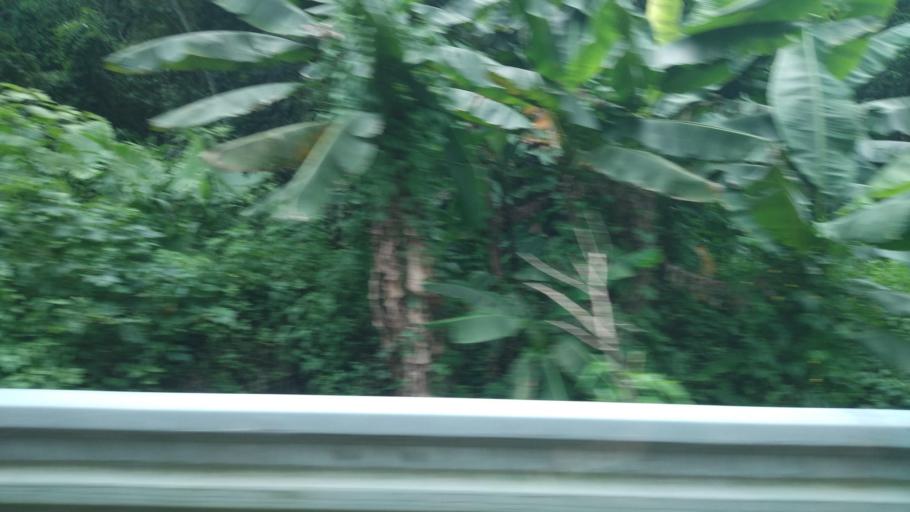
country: TW
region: Taipei
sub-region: Taipei
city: Banqiao
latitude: 24.9212
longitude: 121.4248
